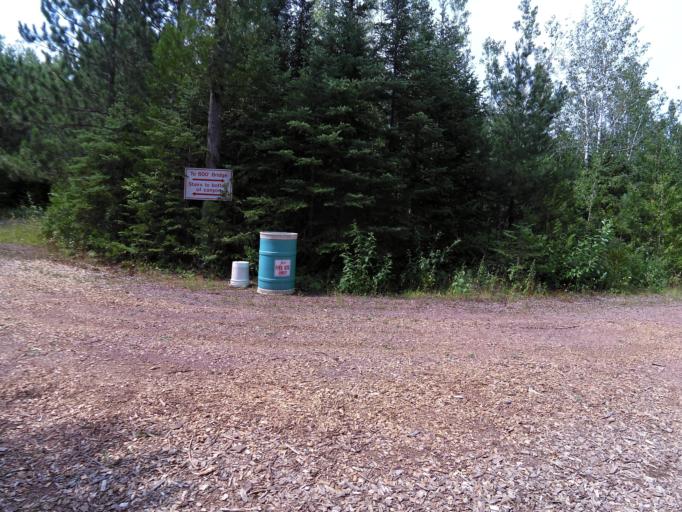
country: CA
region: Ontario
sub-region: Thunder Bay District
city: Thunder Bay
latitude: 48.7998
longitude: -88.6190
